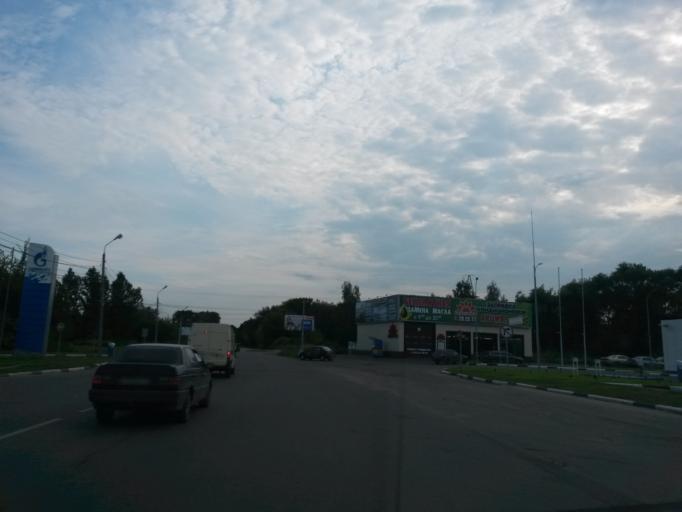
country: RU
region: Jaroslavl
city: Yaroslavl
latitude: 57.6154
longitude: 39.8413
